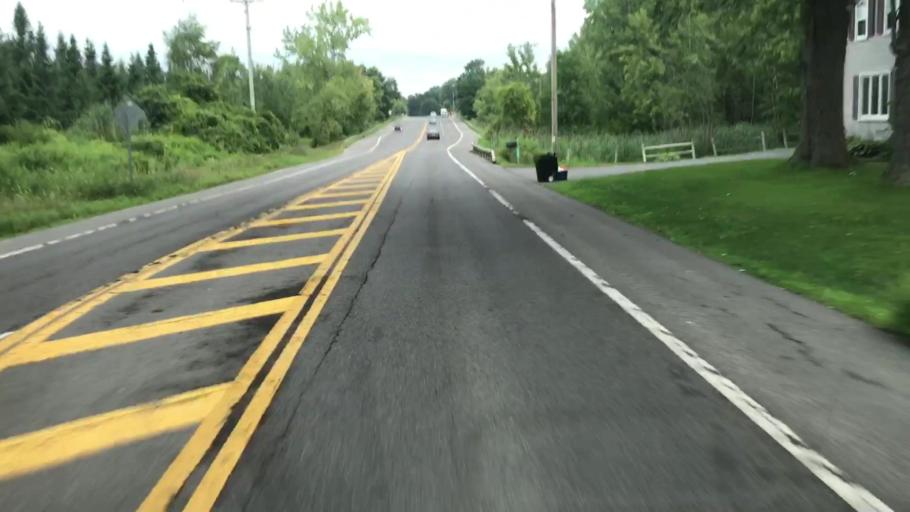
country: US
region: New York
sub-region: Onondaga County
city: Liverpool
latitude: 43.1695
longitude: -76.2090
